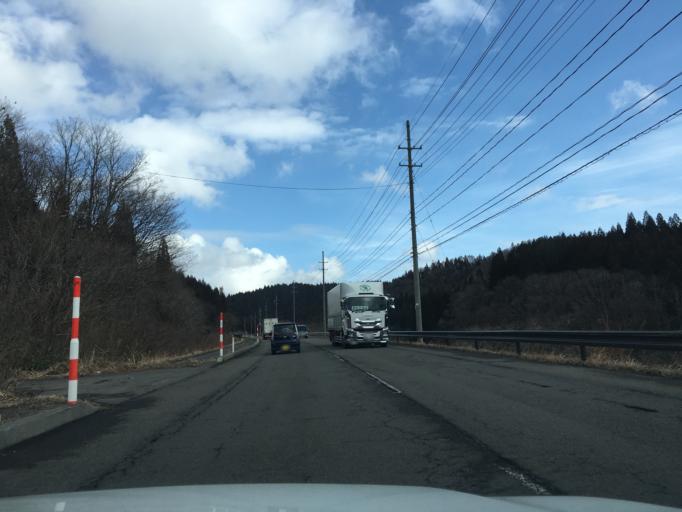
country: JP
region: Akita
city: Takanosu
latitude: 40.0899
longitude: 140.3354
